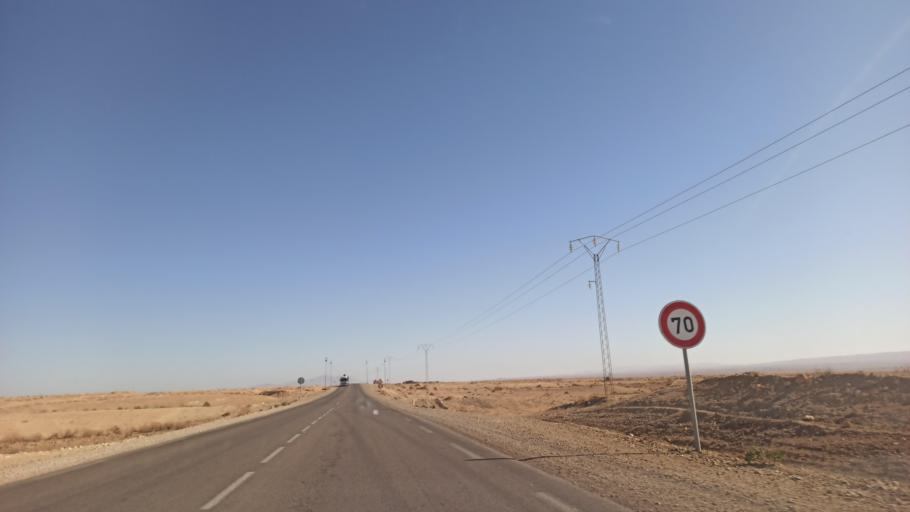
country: TN
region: Gafsa
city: Al Metlaoui
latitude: 34.3134
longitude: 8.4894
